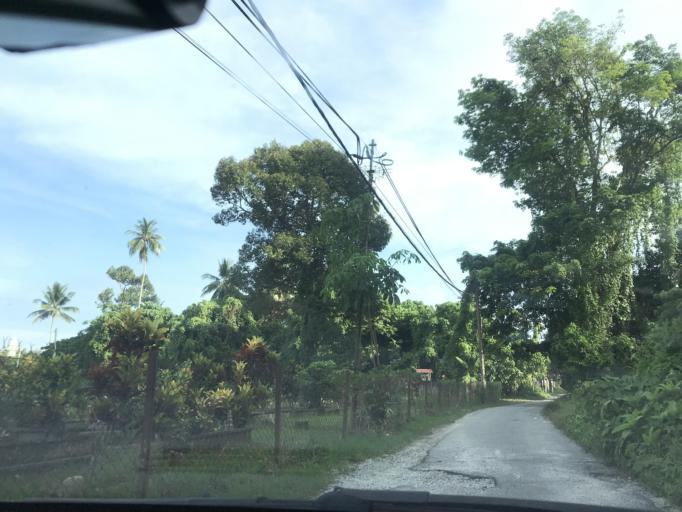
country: MY
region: Kelantan
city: Kota Bharu
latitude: 6.1213
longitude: 102.2218
